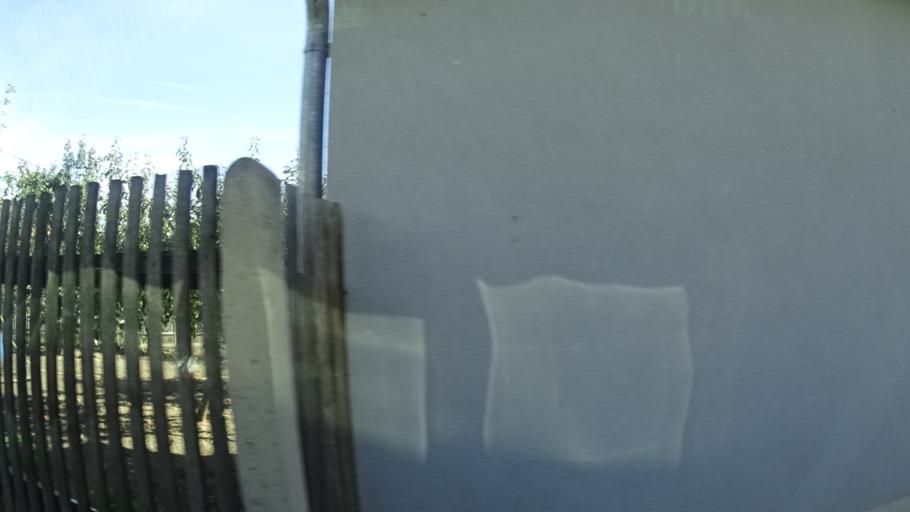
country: DE
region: Thuringia
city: Rittersdorf
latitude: 50.7484
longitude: 11.2125
